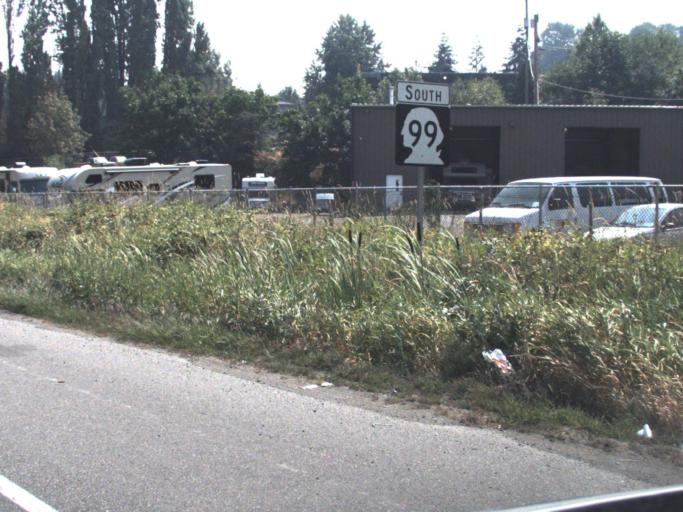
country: US
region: Washington
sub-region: King County
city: Boulevard Park
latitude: 47.5159
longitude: -122.3117
